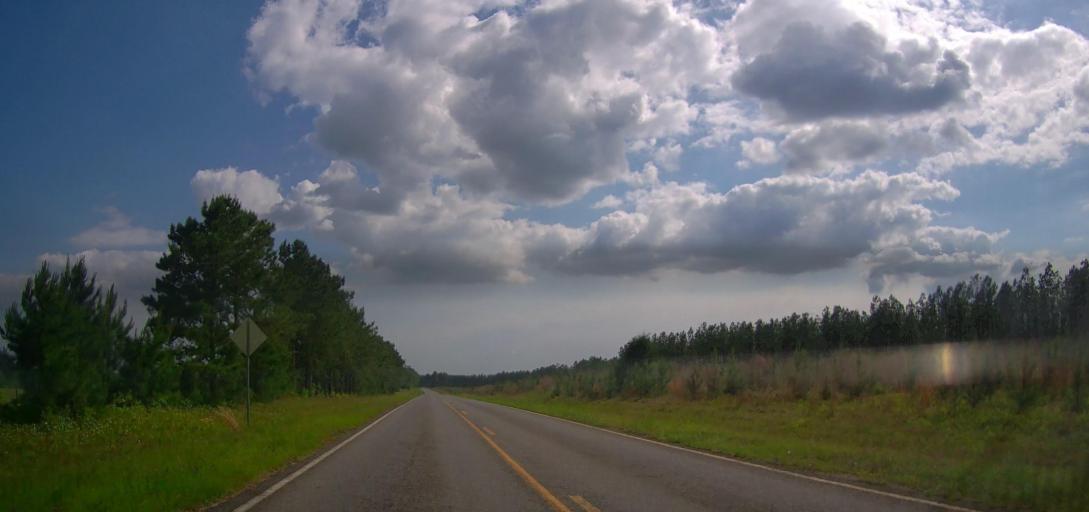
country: US
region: Georgia
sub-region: Laurens County
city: East Dublin
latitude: 32.7171
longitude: -82.9163
